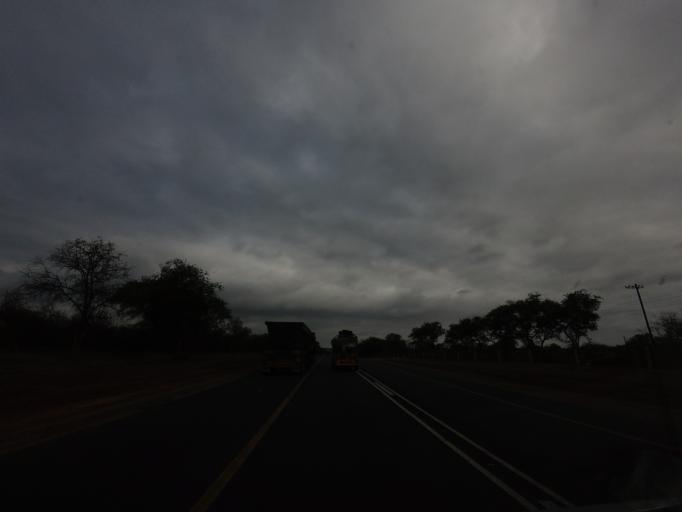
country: ZA
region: Mpumalanga
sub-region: Ehlanzeni District
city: Komatipoort
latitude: -25.4409
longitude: 31.7230
